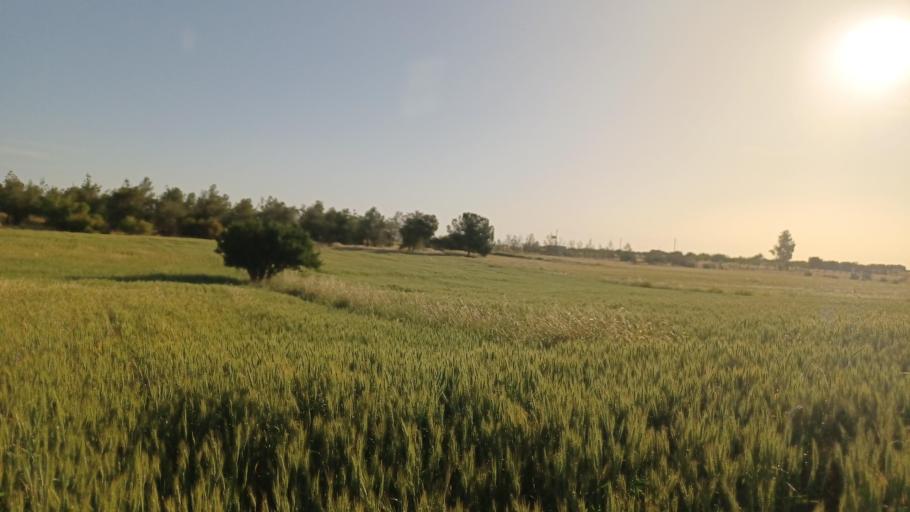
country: CY
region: Lefkosia
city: Kokkinotrimithia
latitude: 35.1510
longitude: 33.1723
